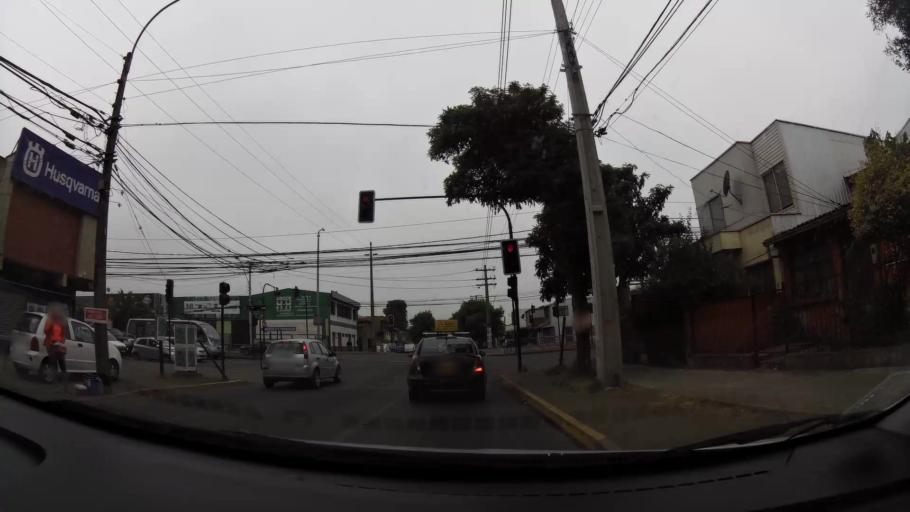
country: CL
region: Biobio
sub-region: Provincia de Concepcion
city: Concepcion
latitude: -36.8098
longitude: -73.0511
